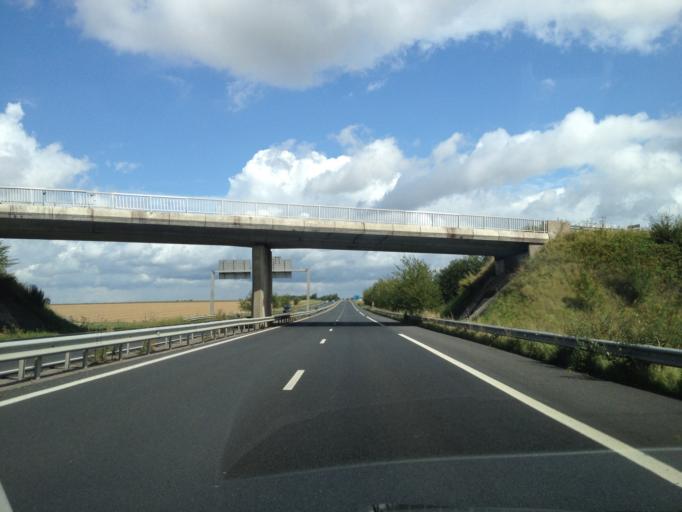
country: FR
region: Haute-Normandie
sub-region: Departement de la Seine-Maritime
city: Saint-Martin-Osmonville
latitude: 49.5796
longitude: 1.2760
